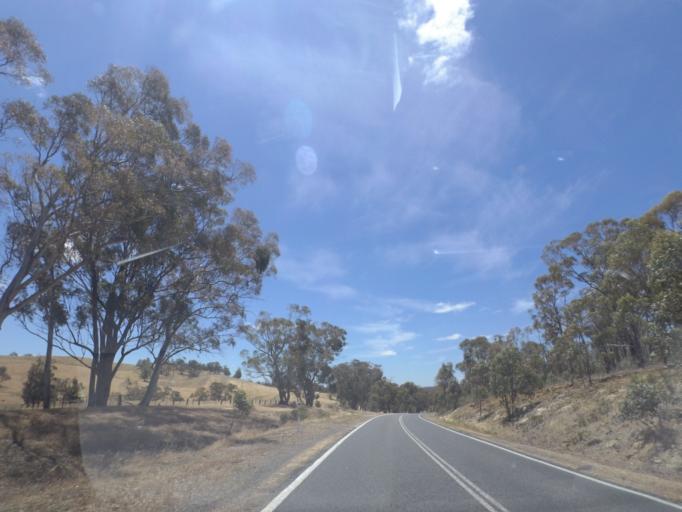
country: AU
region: Victoria
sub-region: Mount Alexander
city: Castlemaine
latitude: -37.2049
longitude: 144.1411
